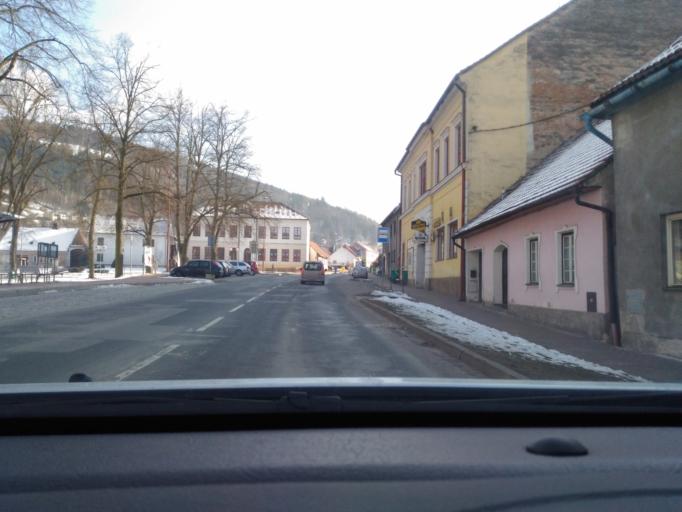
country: CZ
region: South Moravian
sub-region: Okres Brno-Venkov
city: Nedvedice
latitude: 49.4248
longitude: 16.3515
